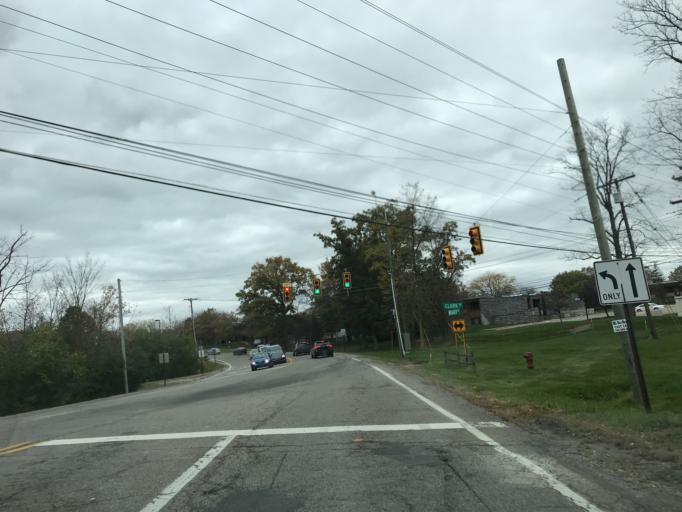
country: US
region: Michigan
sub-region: Washtenaw County
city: Ann Arbor
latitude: 42.2593
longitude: -83.6803
